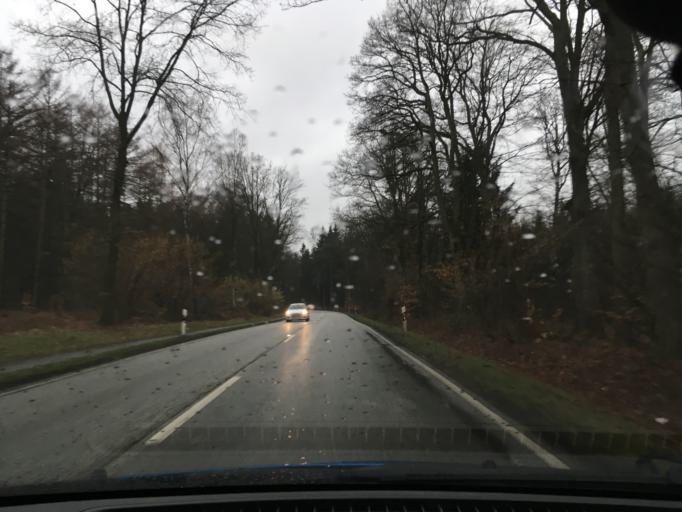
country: DE
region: Schleswig-Holstein
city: Schnakenbek
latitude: 53.3934
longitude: 10.4792
